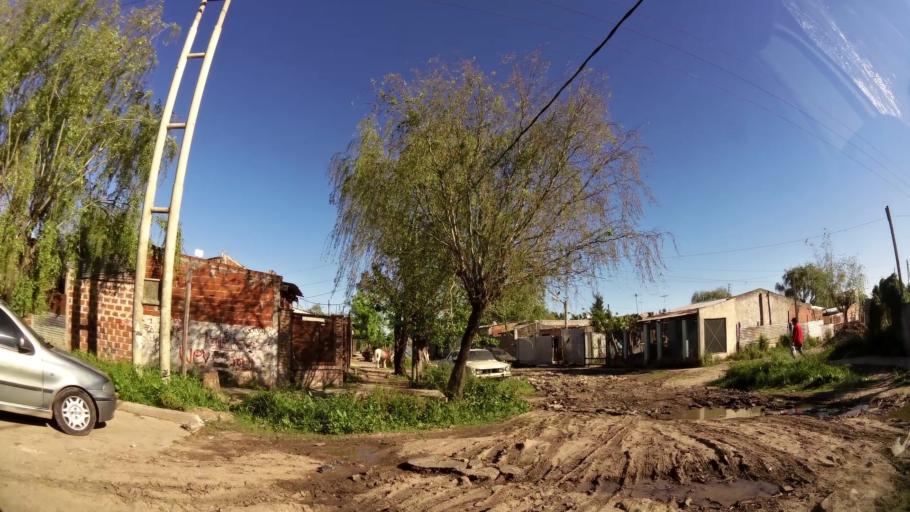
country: AR
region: Buenos Aires
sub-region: Partido de Almirante Brown
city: Adrogue
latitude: -34.7591
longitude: -58.3204
